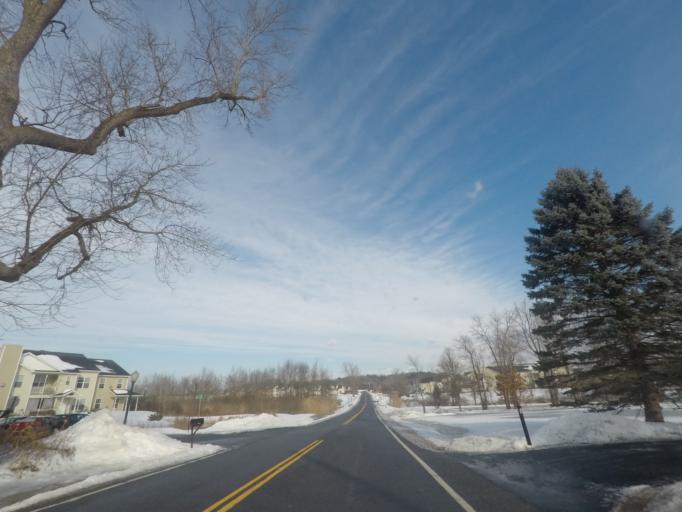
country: US
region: New York
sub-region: Saratoga County
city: Mechanicville
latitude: 42.8588
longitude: -73.7355
